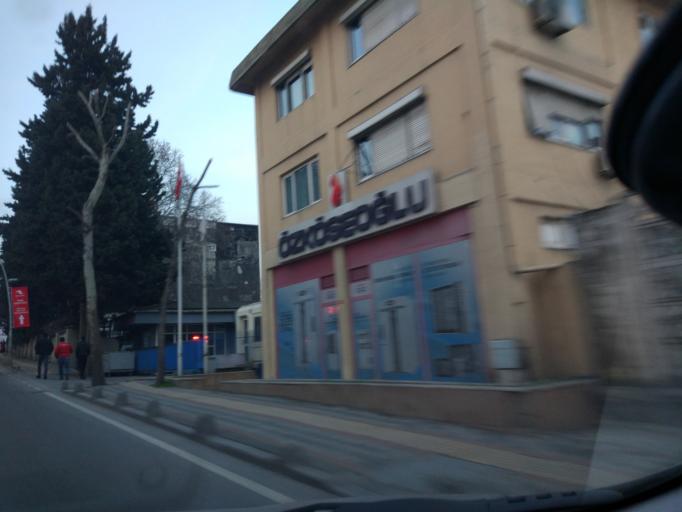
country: TR
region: Istanbul
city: Bahcelievler
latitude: 41.0099
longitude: 28.8227
